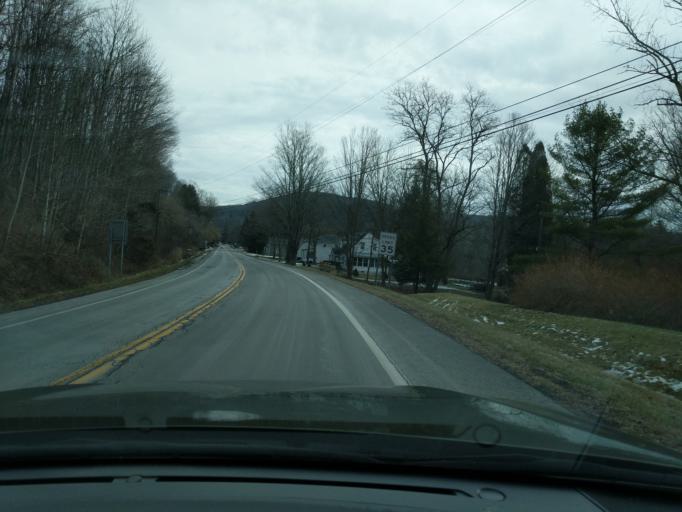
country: US
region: New York
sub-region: Tompkins County
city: East Ithaca
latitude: 42.3834
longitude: -76.4019
